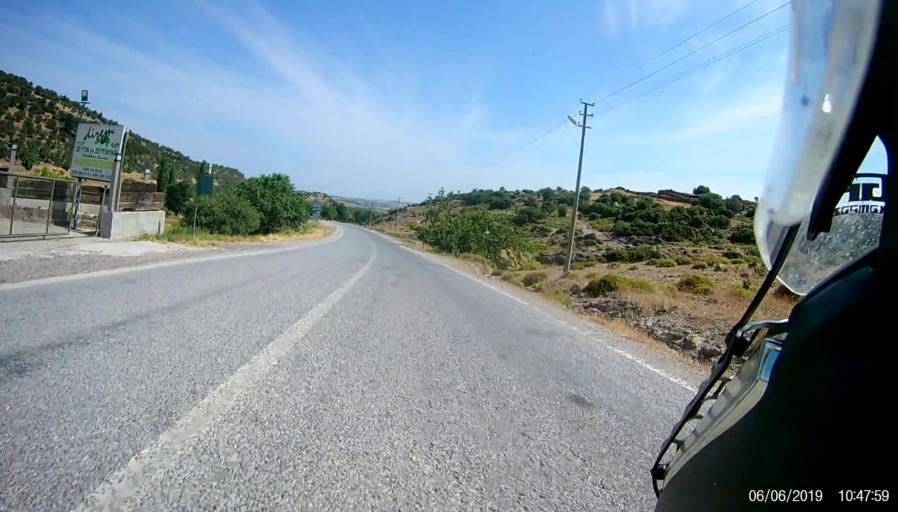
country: TR
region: Canakkale
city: Ayvacik
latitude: 39.5226
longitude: 26.4644
